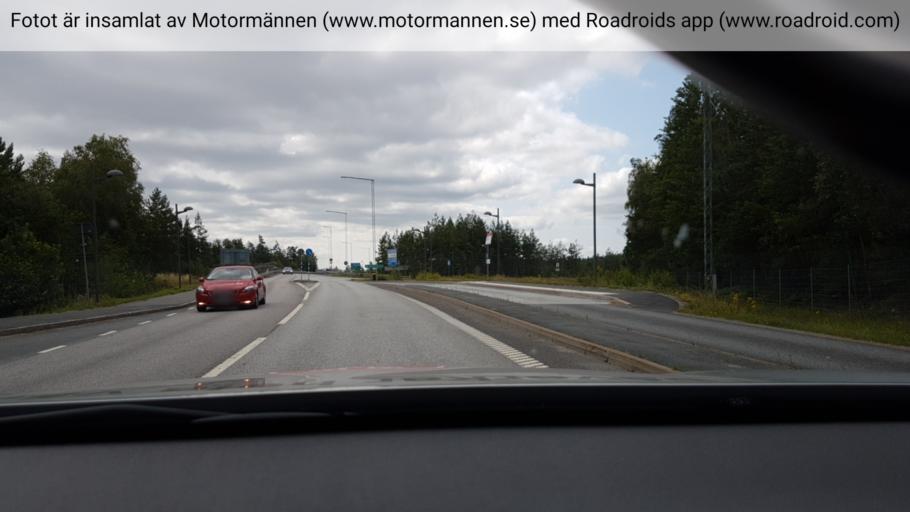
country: SE
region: Stockholm
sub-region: Norrtalje Kommun
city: Rimbo
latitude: 59.6381
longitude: 18.3325
